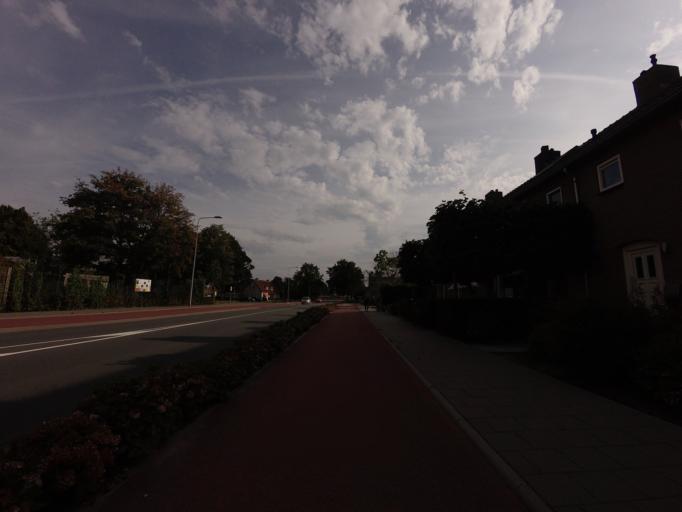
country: NL
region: South Holland
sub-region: Gemeente Papendrecht
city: Papendrecht
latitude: 51.8282
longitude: 4.6931
